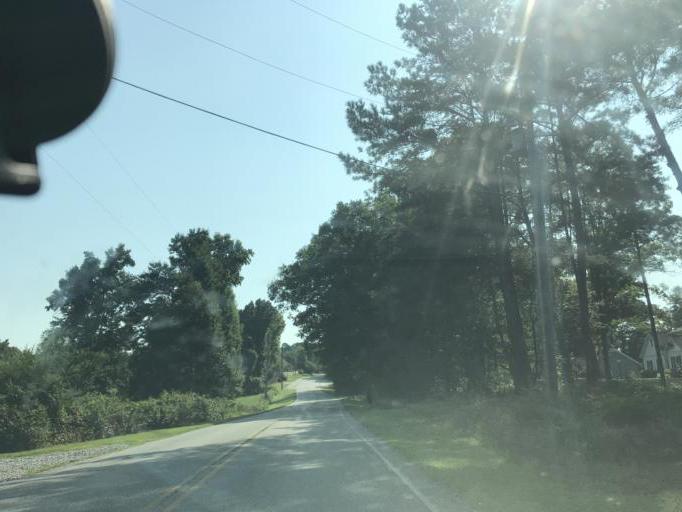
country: US
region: Georgia
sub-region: Forsyth County
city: Cumming
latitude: 34.2321
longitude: -84.1135
